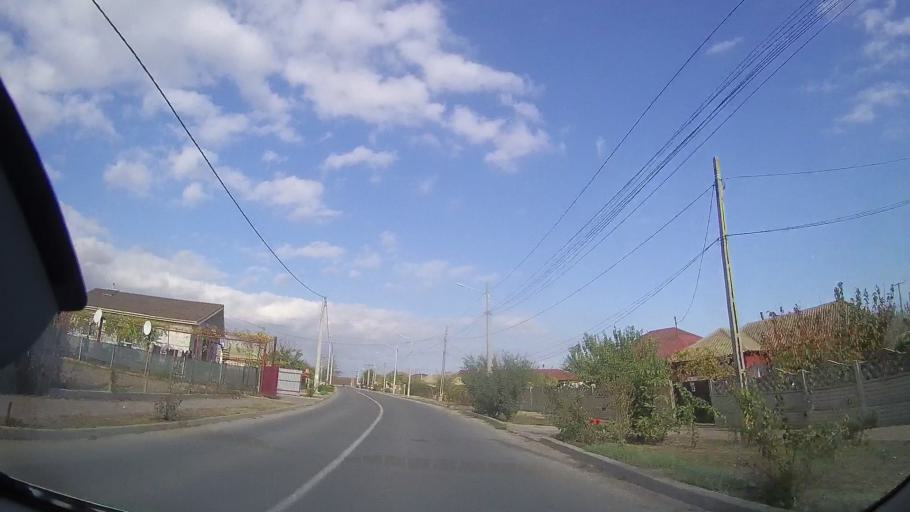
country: RO
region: Constanta
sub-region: Comuna Douazeci si Trei August
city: Dulcesti
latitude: 43.9082
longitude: 28.5490
